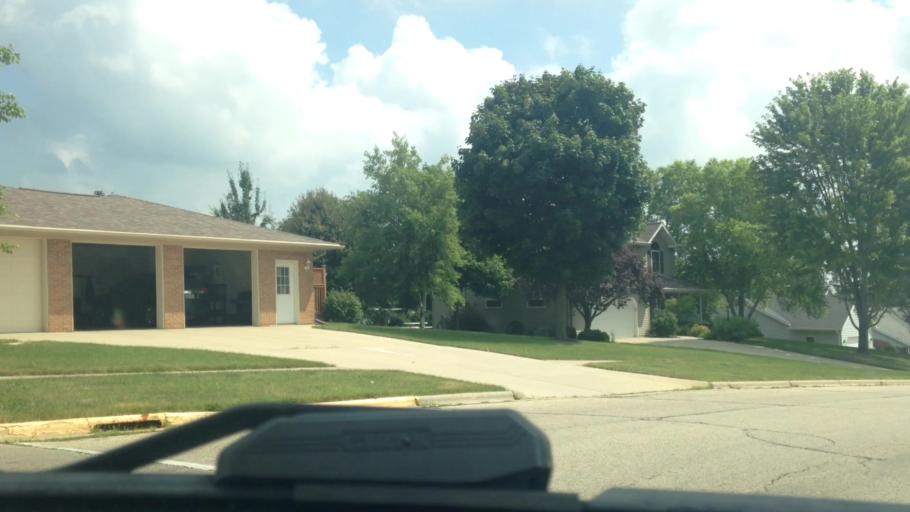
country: US
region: Wisconsin
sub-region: Dodge County
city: Mayville
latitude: 43.4976
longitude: -88.5662
